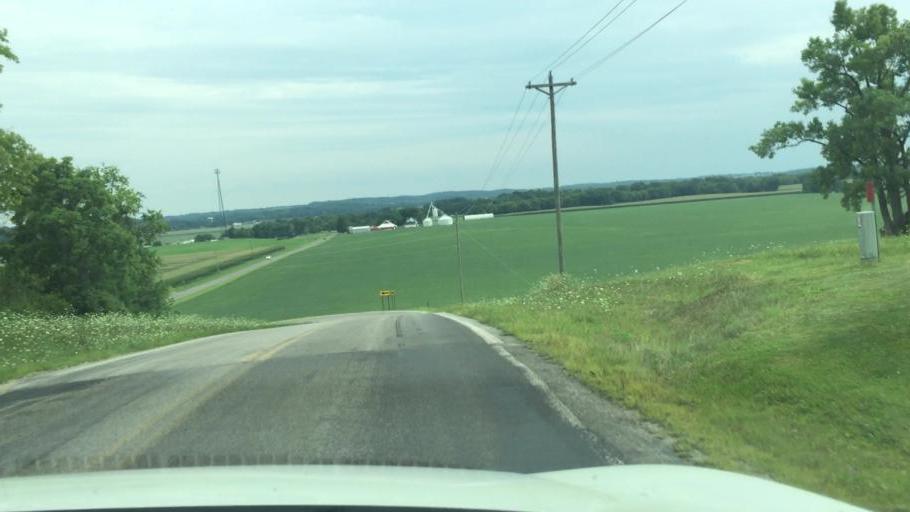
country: US
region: Ohio
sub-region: Champaign County
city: Mechanicsburg
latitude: 40.0409
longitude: -83.6566
